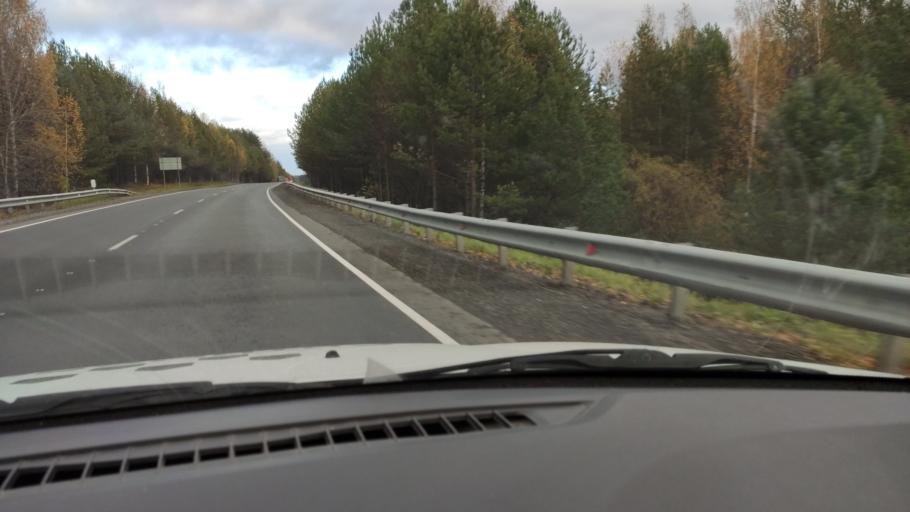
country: RU
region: Kirov
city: Belaya Kholunitsa
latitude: 58.8945
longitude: 50.8932
